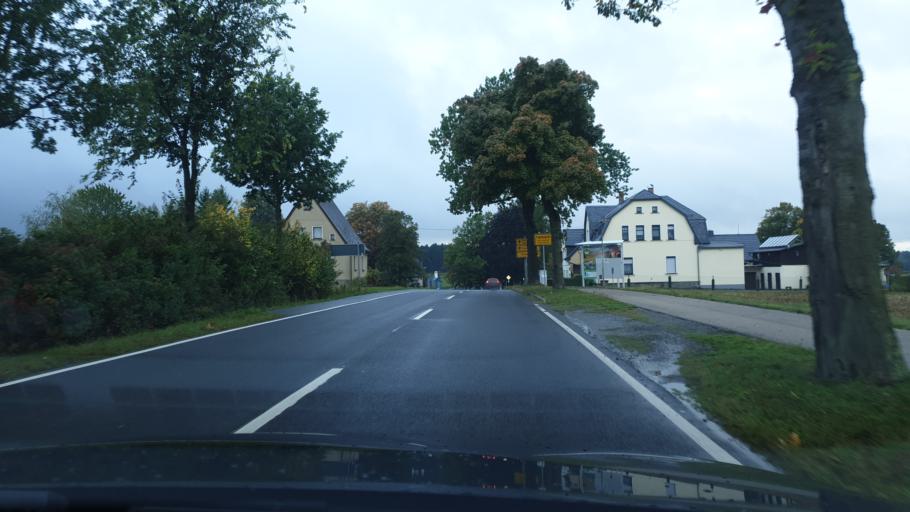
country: DE
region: Saxony
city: Neustadt Vogtland
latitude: 50.4557
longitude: 12.3277
